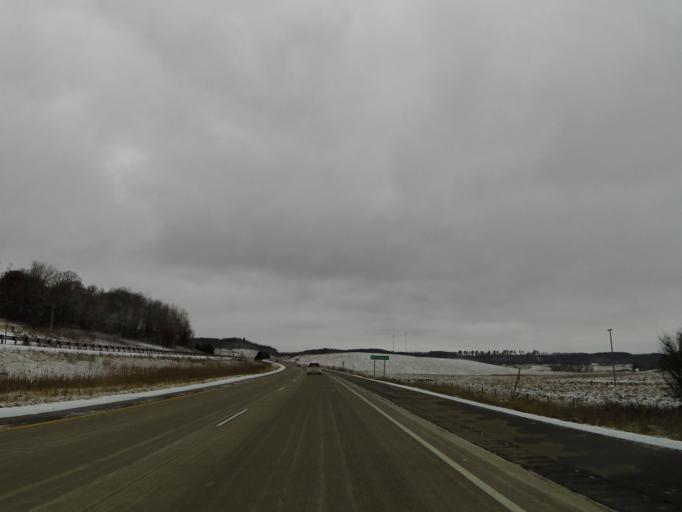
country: US
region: Wisconsin
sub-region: Trempealeau County
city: Osseo
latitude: 44.5965
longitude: -91.2177
